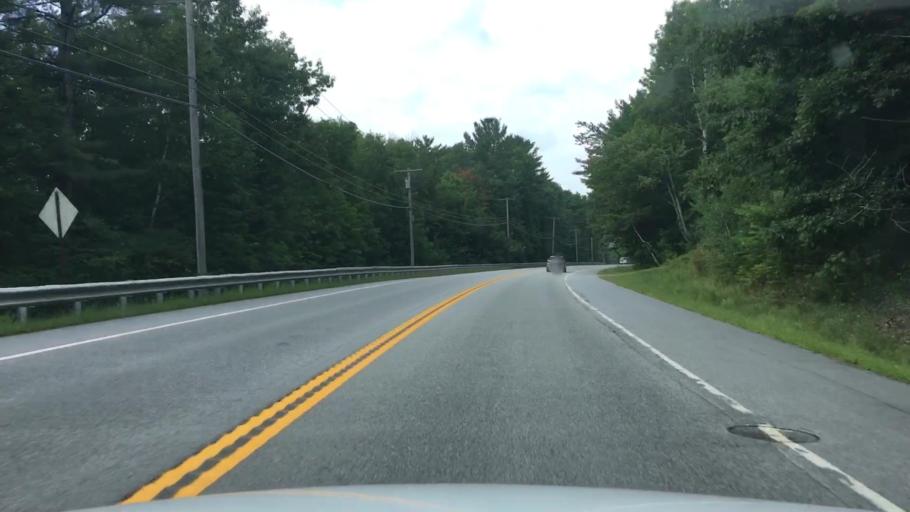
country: US
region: Maine
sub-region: Oxford County
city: Rumford
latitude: 44.5087
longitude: -70.6055
